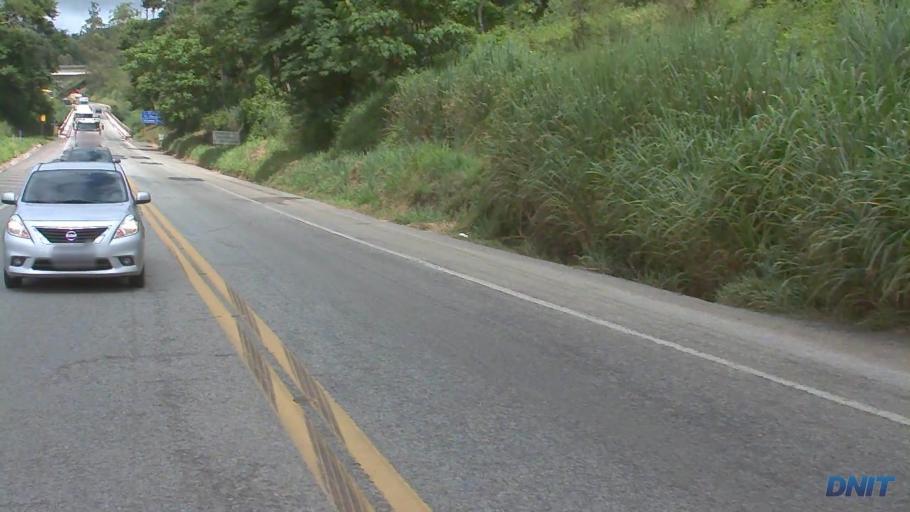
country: BR
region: Minas Gerais
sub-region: Joao Monlevade
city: Joao Monlevade
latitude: -19.8523
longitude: -43.1384
